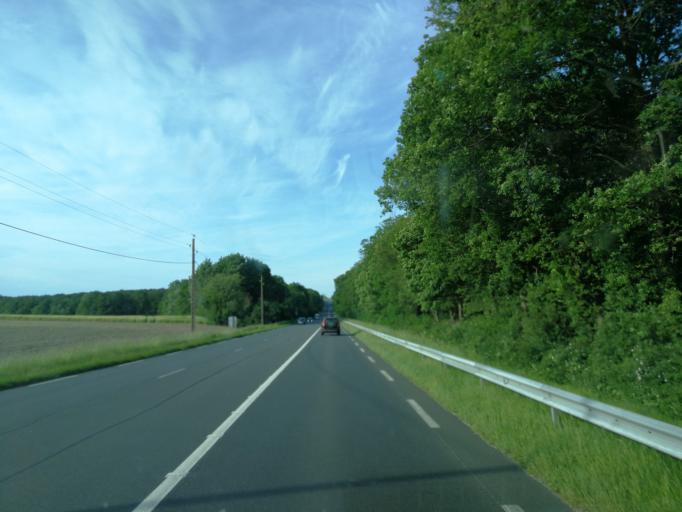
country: FR
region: Centre
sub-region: Departement d'Eure-et-Loir
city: Marboue
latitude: 48.1349
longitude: 1.3414
